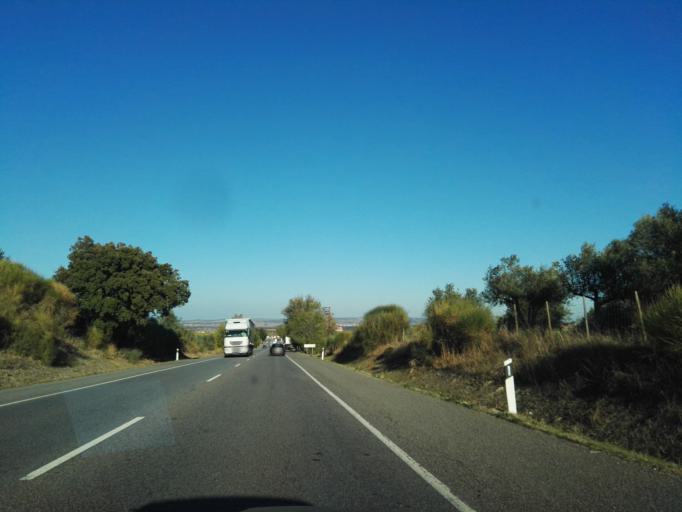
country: PT
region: Evora
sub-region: Borba
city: Borba
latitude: 38.8114
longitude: -7.4550
